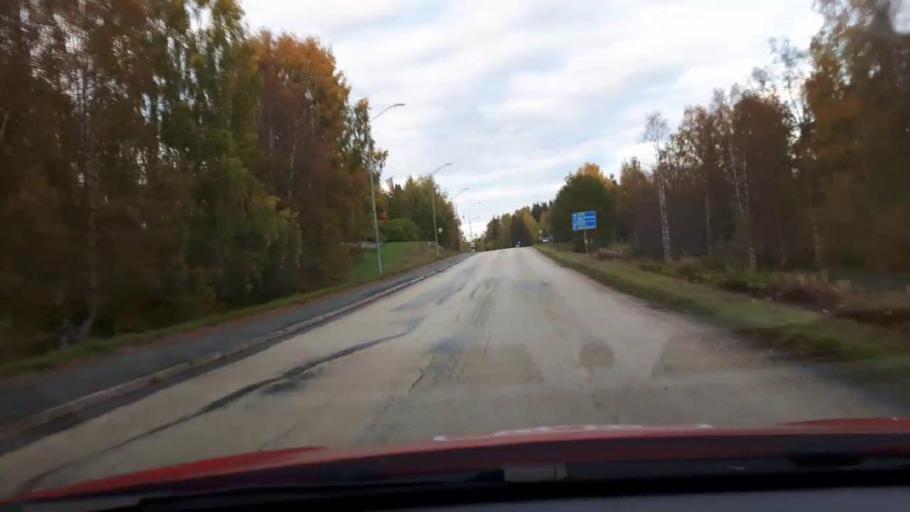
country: SE
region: Jaemtland
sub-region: OEstersunds Kommun
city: Lit
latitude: 63.3193
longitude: 14.8571
